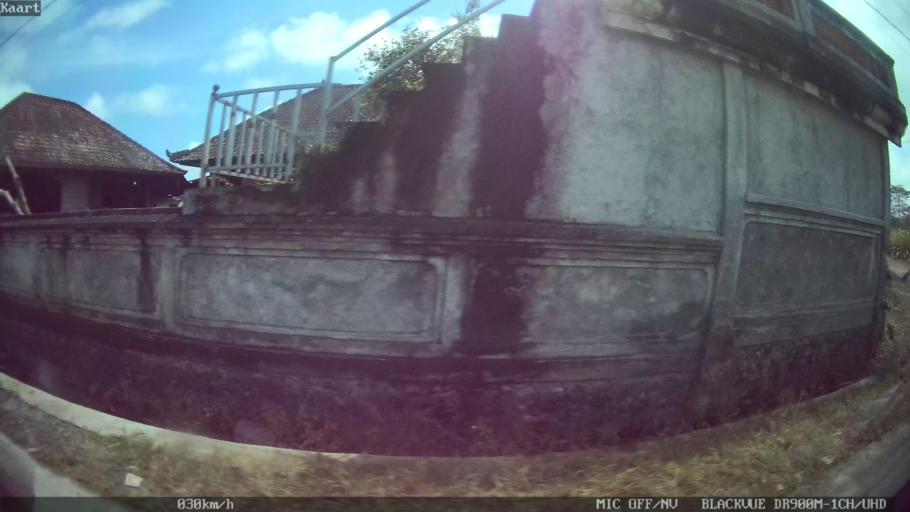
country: ID
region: Bali
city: Banjar Apuan Kaja
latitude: -8.4960
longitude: 115.3414
